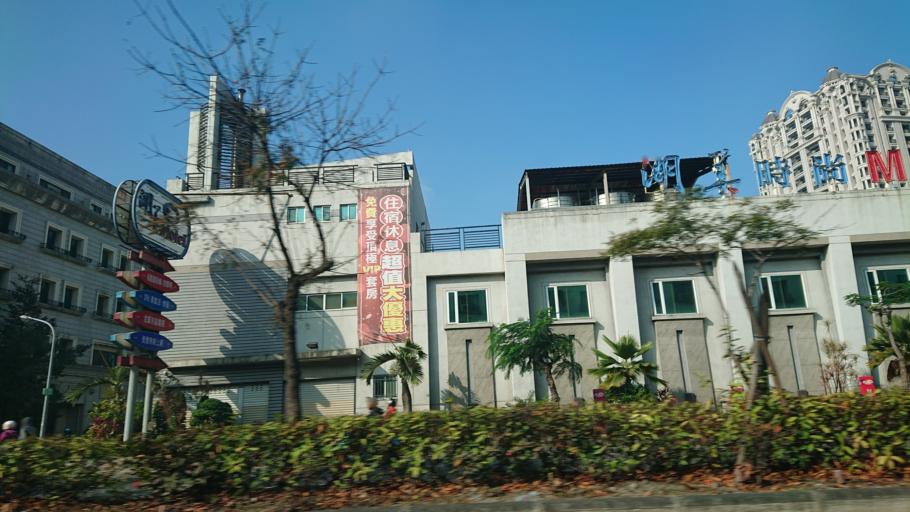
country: TW
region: Taiwan
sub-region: Tainan
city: Tainan
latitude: 23.0049
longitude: 120.1867
